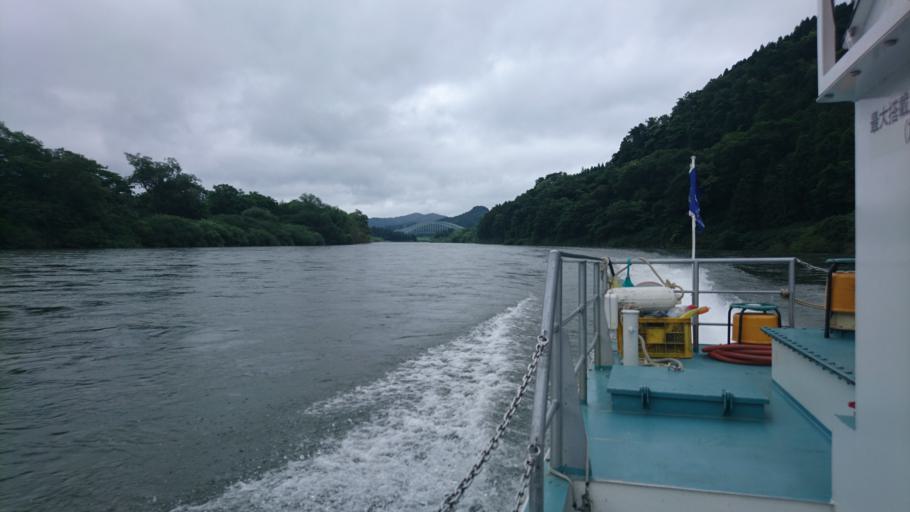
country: JP
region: Iwate
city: Ichinoseki
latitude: 38.9051
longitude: 141.2476
